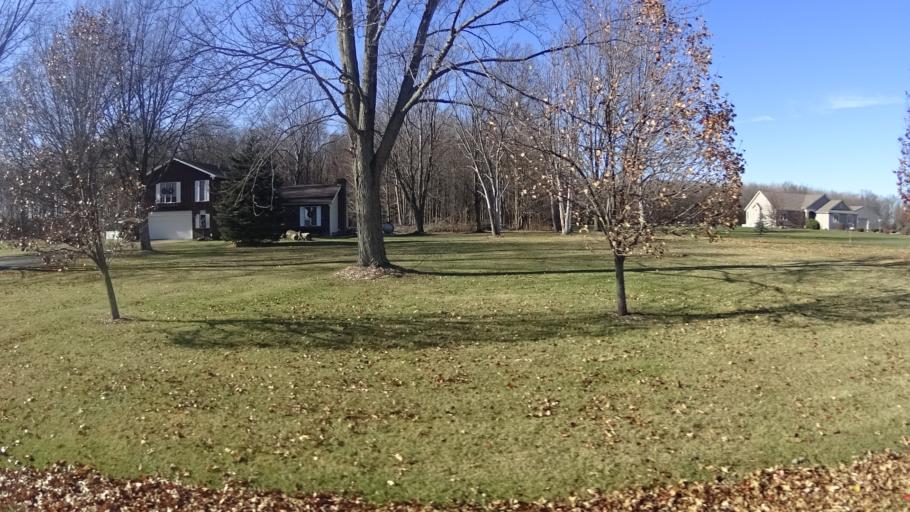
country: US
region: Ohio
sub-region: Lorain County
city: Camden
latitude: 41.2982
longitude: -82.2880
